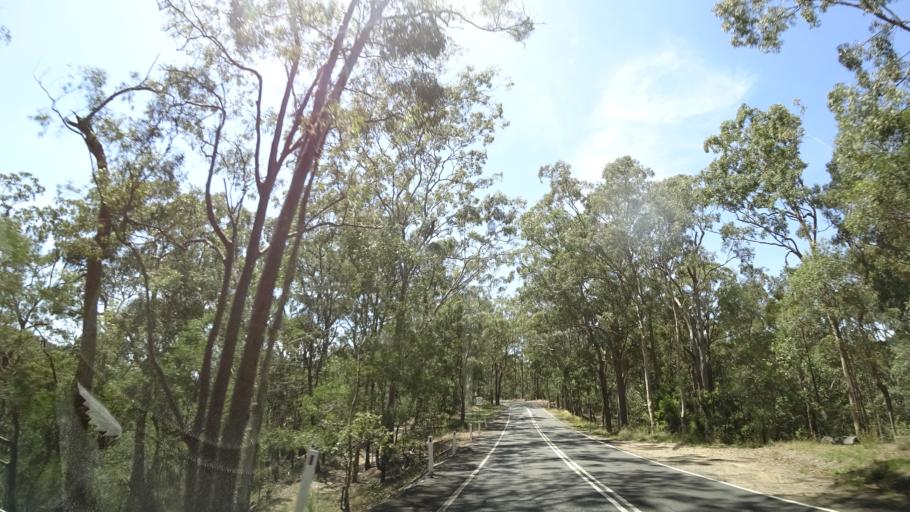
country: AU
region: Queensland
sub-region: Moreton Bay
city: Samford Valley
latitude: -27.4184
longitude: 152.8736
